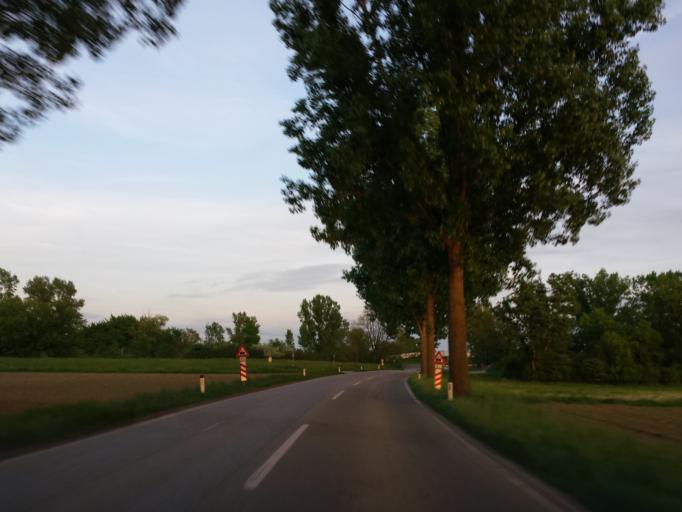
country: AT
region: Lower Austria
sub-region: Politischer Bezirk Tulln
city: Michelhausen
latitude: 48.3372
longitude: 15.9386
